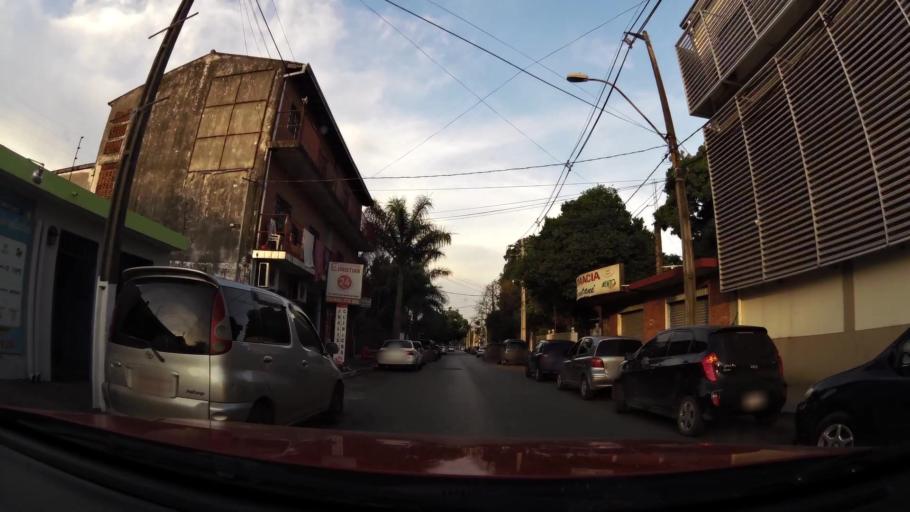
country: PY
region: Central
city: San Lorenzo
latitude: -25.3409
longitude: -57.5070
